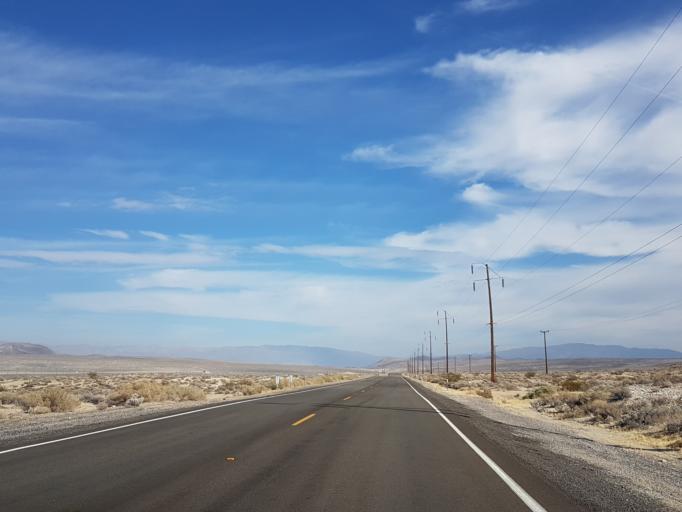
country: US
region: California
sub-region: Kern County
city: Ridgecrest
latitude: 35.6460
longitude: -117.5191
